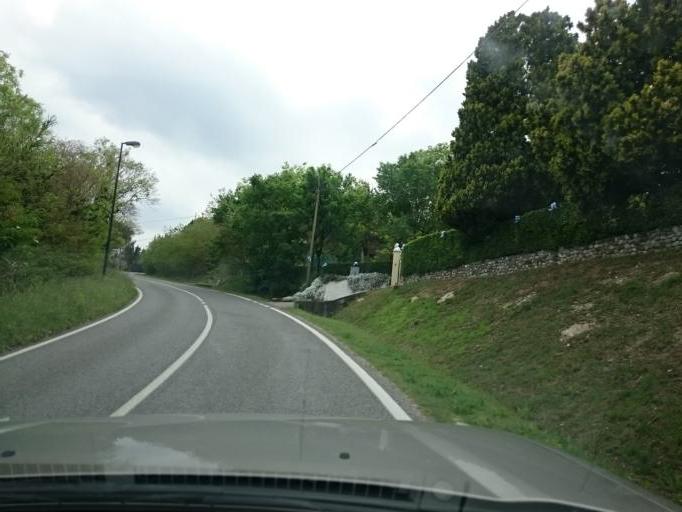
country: IT
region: Veneto
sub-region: Provincia di Padova
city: Arqua Petrarca
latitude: 45.2646
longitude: 11.7025
